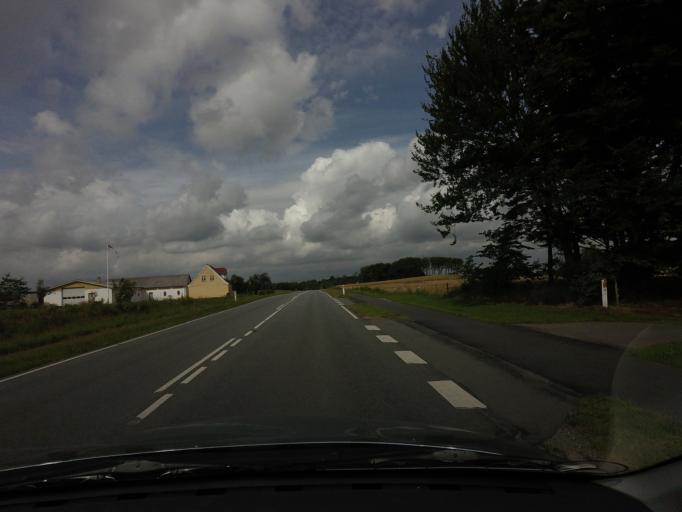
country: DK
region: North Denmark
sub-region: Hjorring Kommune
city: Tars
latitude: 57.3805
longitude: 10.1385
